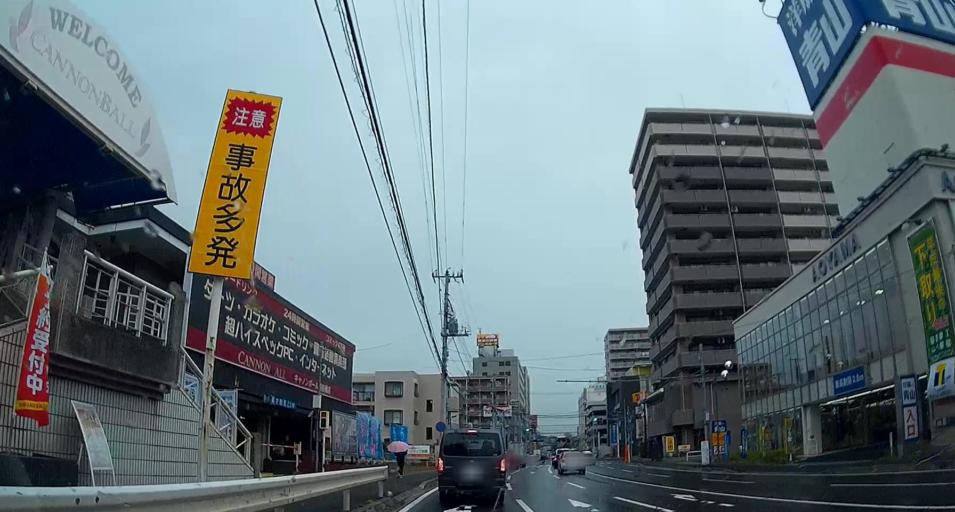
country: JP
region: Chiba
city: Funabashi
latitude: 35.7074
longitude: 139.9529
